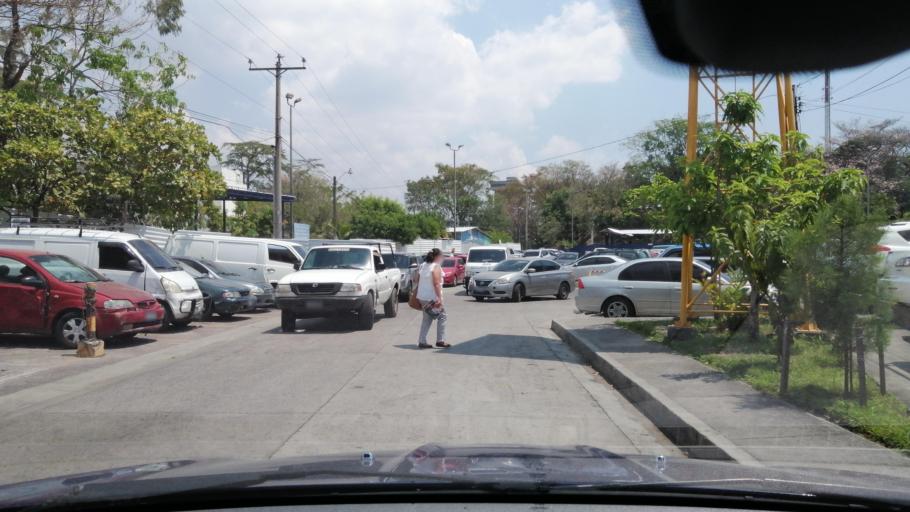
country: SV
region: San Salvador
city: San Salvador
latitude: 13.7038
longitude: -89.2034
